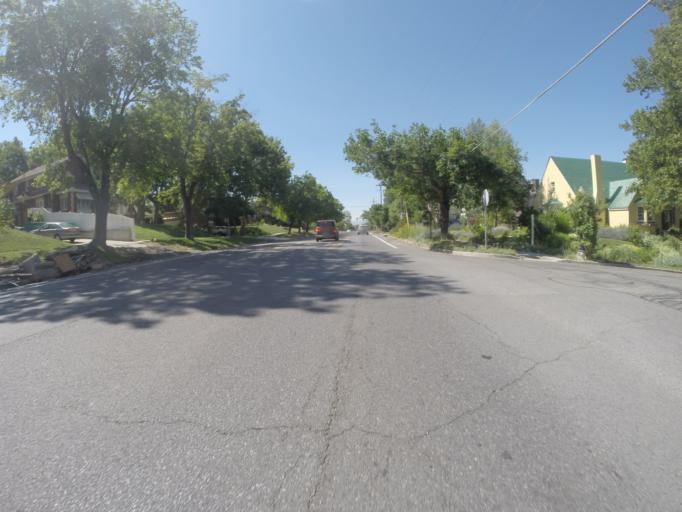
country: US
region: Utah
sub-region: Salt Lake County
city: Willard
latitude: 40.7430
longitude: -111.8539
